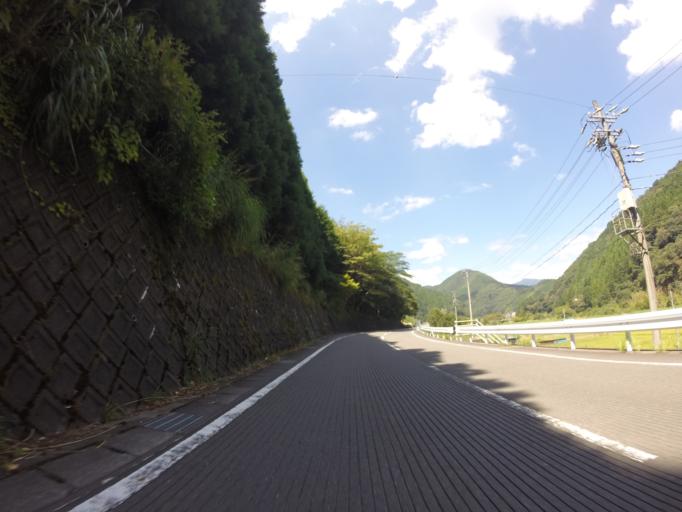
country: JP
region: Shizuoka
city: Shizuoka-shi
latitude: 35.0615
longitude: 138.2468
